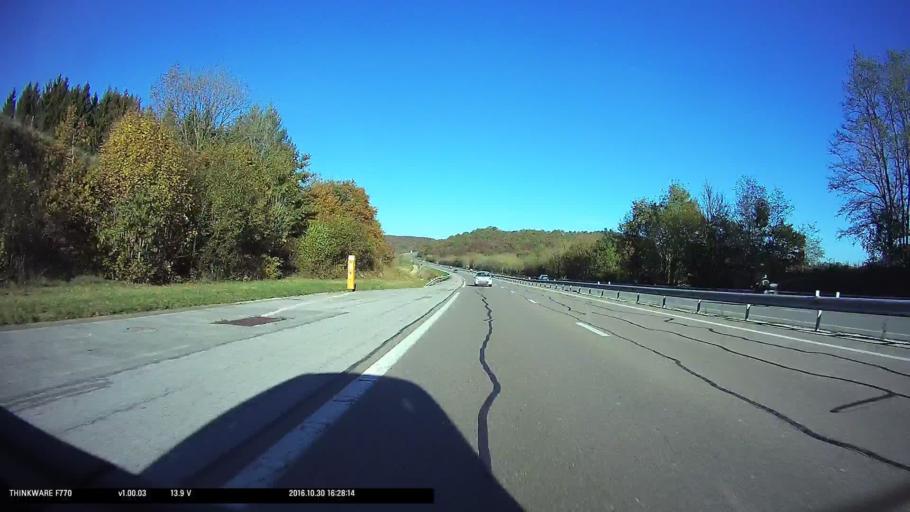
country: FR
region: Franche-Comte
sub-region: Departement du Doubs
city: Baume-les-Dames
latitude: 47.3420
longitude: 6.2947
